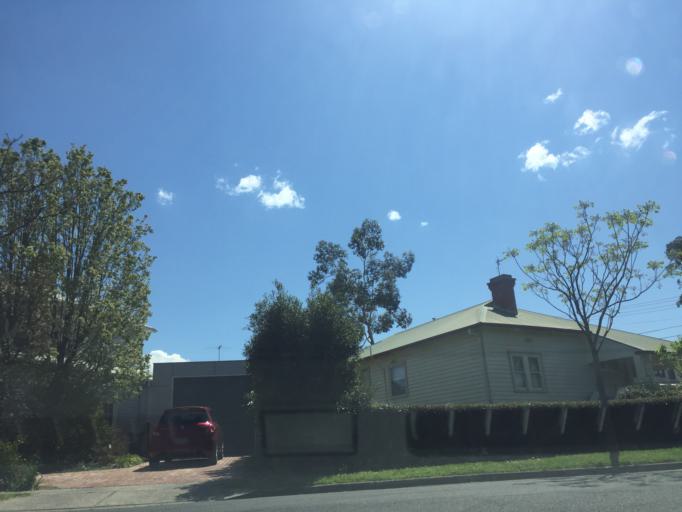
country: AU
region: Victoria
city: Alphington
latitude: -37.7861
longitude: 145.0322
